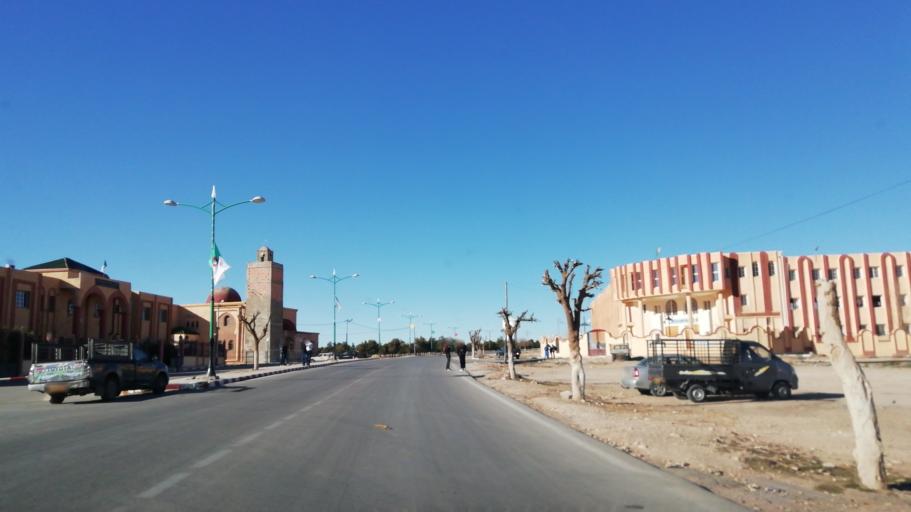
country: DZ
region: Tlemcen
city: Sebdou
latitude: 34.2267
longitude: -1.2554
